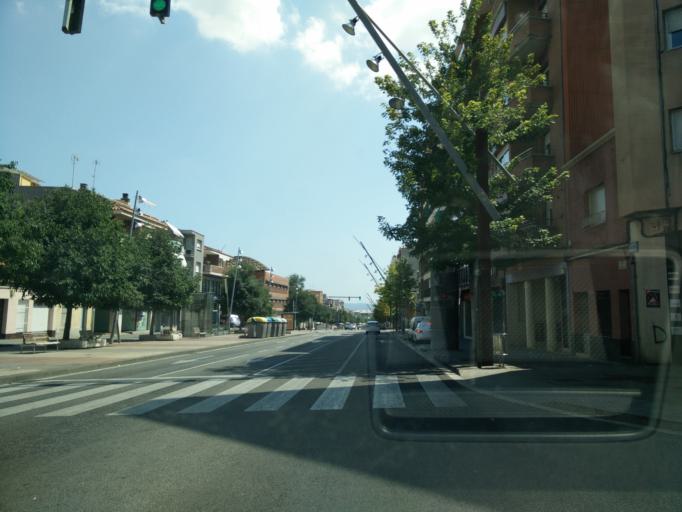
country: ES
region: Catalonia
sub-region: Provincia de Barcelona
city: Terrassa
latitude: 41.5656
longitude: 2.0269
